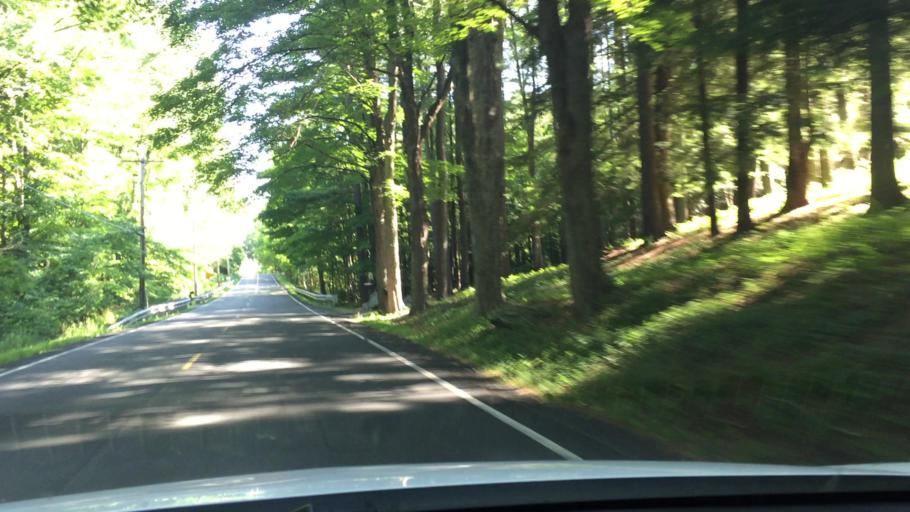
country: US
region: Massachusetts
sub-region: Berkshire County
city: West Stockbridge
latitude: 42.3029
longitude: -73.3733
